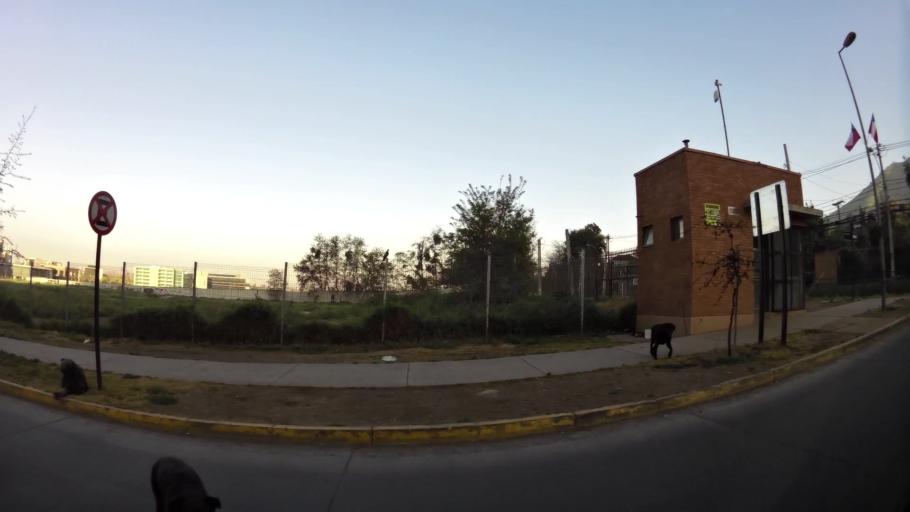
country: CL
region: Santiago Metropolitan
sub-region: Provincia de Santiago
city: Santiago
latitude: -33.3844
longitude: -70.6149
